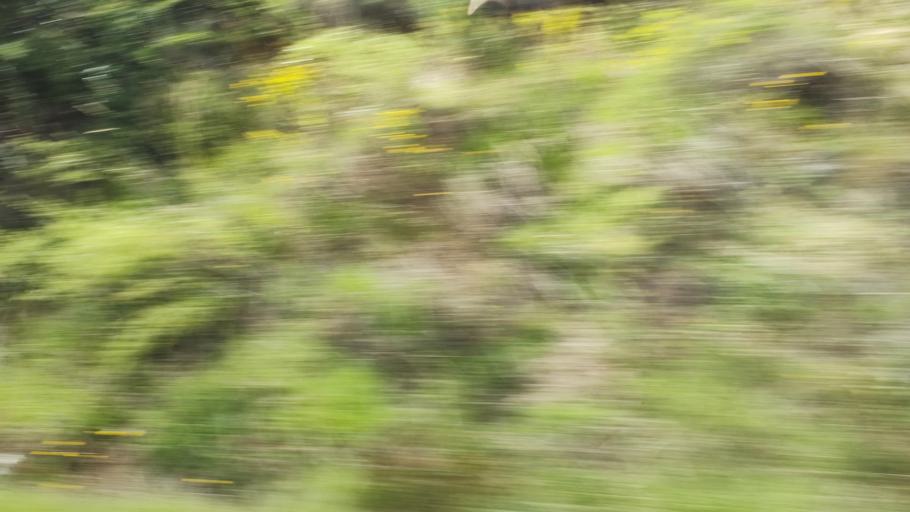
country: RO
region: Mehedinti
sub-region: Comuna Eselnita
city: Eselnita
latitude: 44.6827
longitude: 22.3589
